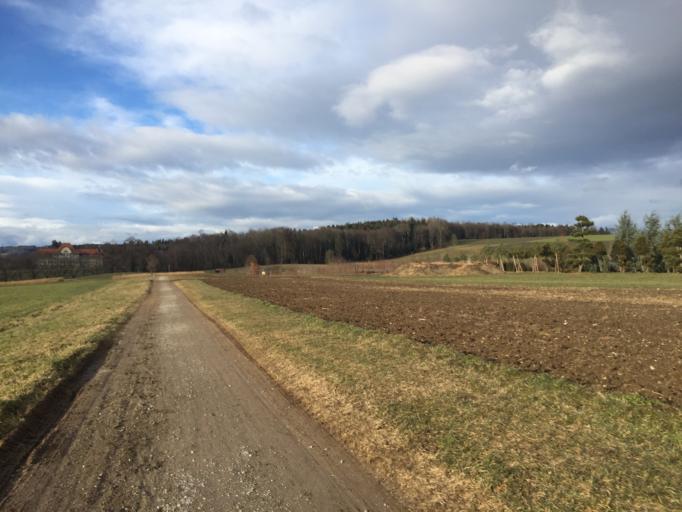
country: CH
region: Bern
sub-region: Bern-Mittelland District
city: Munsingen
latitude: 46.8831
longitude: 7.5603
